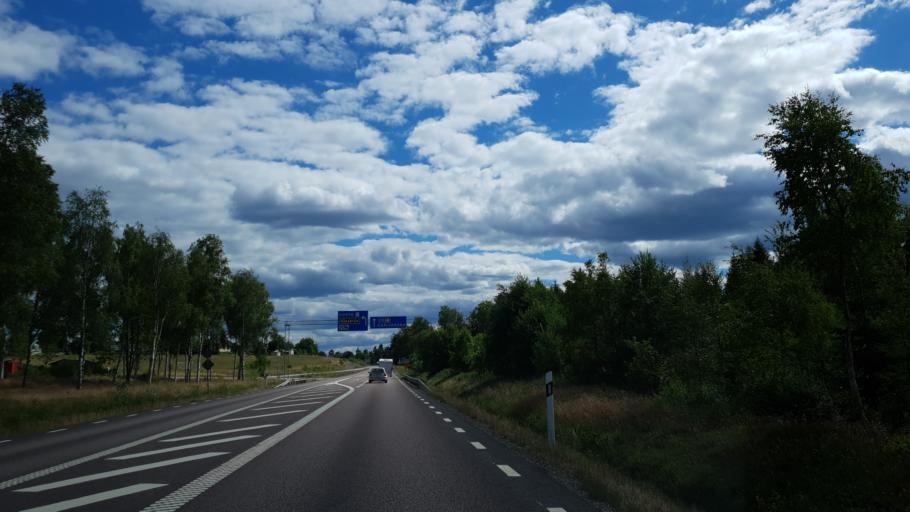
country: SE
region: Kronoberg
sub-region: Lessebo Kommun
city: Lessebo
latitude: 56.8509
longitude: 15.3887
